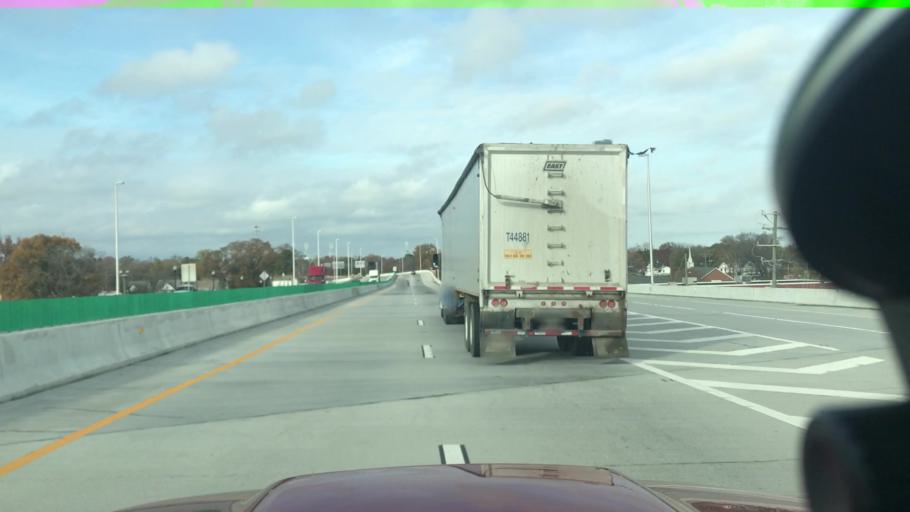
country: US
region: Virginia
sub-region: City of Portsmouth
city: Portsmouth
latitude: 36.8318
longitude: -76.3269
